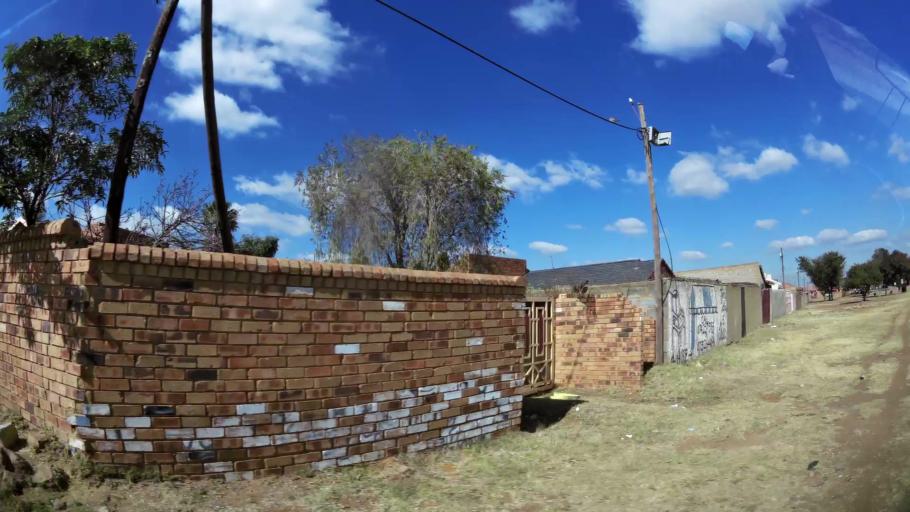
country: ZA
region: Gauteng
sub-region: West Rand District Municipality
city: Krugersdorp
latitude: -26.1379
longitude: 27.7959
